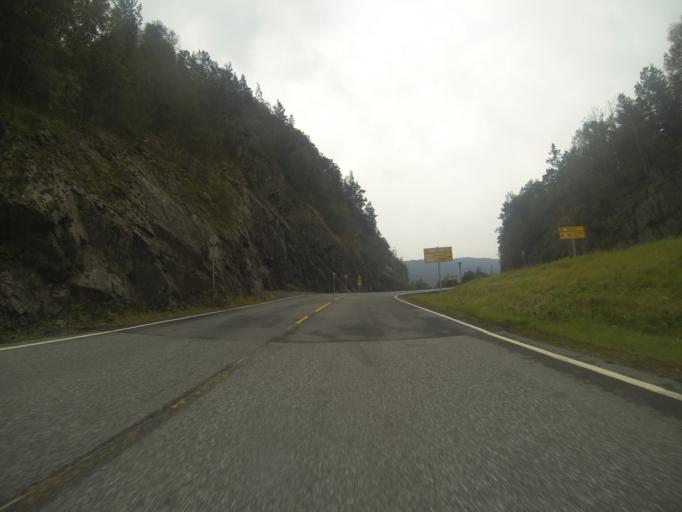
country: NO
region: Rogaland
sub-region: Suldal
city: Sand
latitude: 59.4834
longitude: 6.2008
